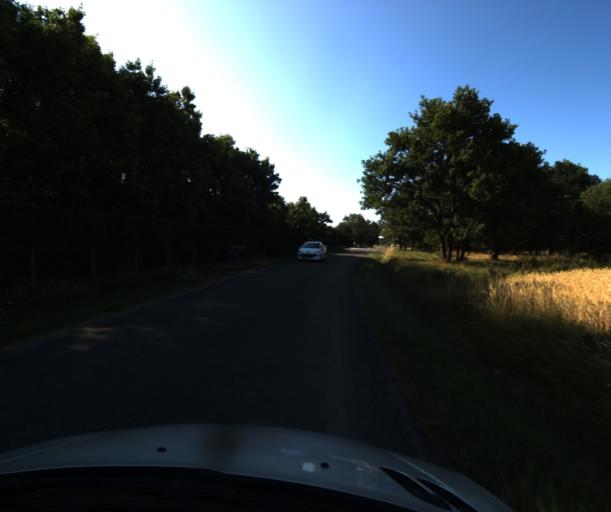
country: FR
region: Midi-Pyrenees
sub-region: Departement du Tarn-et-Garonne
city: Saint-Porquier
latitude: 44.0451
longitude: 1.2147
